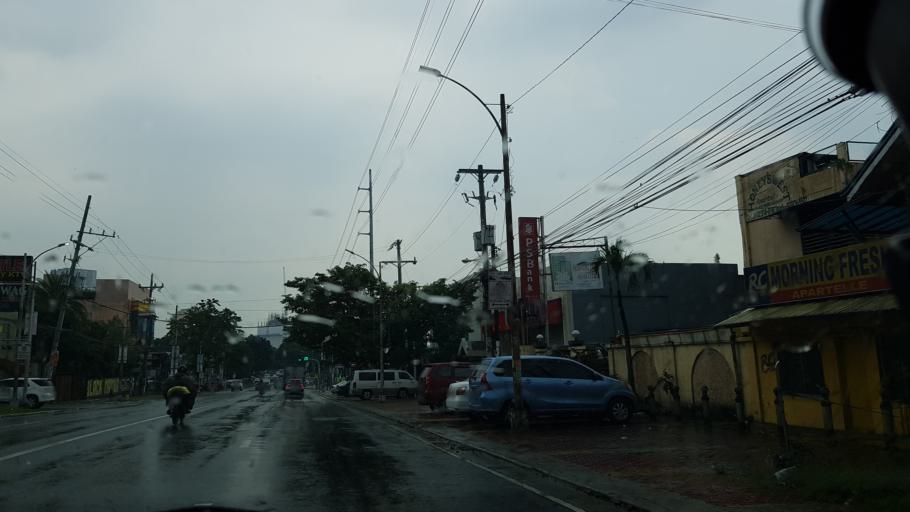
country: PH
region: Calabarzon
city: Del Monte
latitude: 14.6439
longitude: 121.0273
